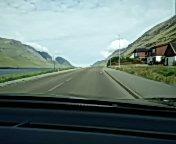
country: FO
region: Nordoyar
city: Klaksvik
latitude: 62.3003
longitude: -6.5220
